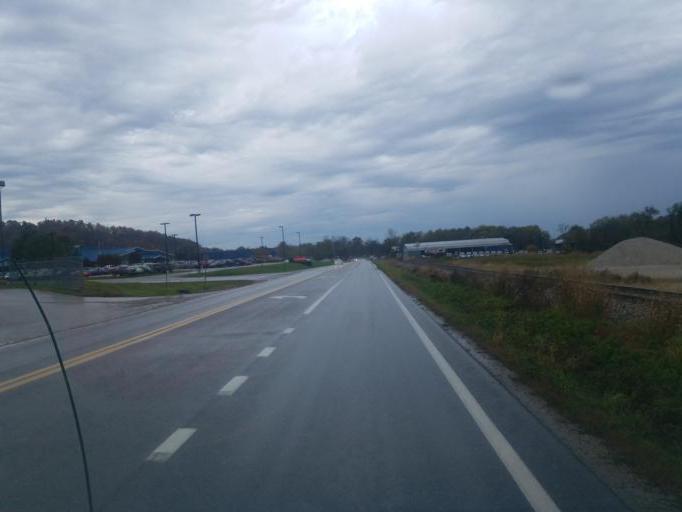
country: US
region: West Virginia
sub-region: Wood County
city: Williamstown
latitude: 39.3957
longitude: -81.4696
